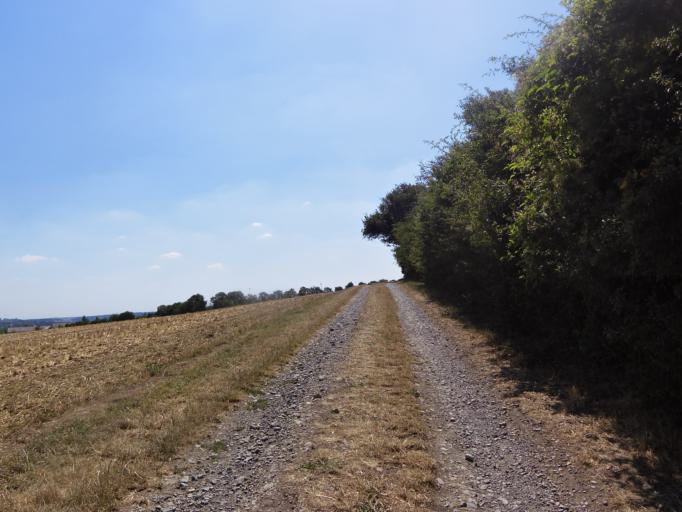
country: DE
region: Bavaria
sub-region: Regierungsbezirk Unterfranken
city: Wuerzburg
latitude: 49.8116
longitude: 9.9509
